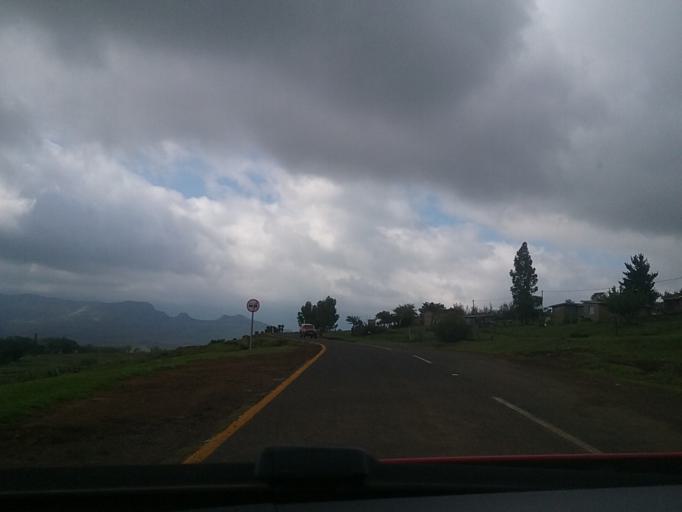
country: LS
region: Berea
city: Teyateyaneng
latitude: -29.2503
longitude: 27.8465
